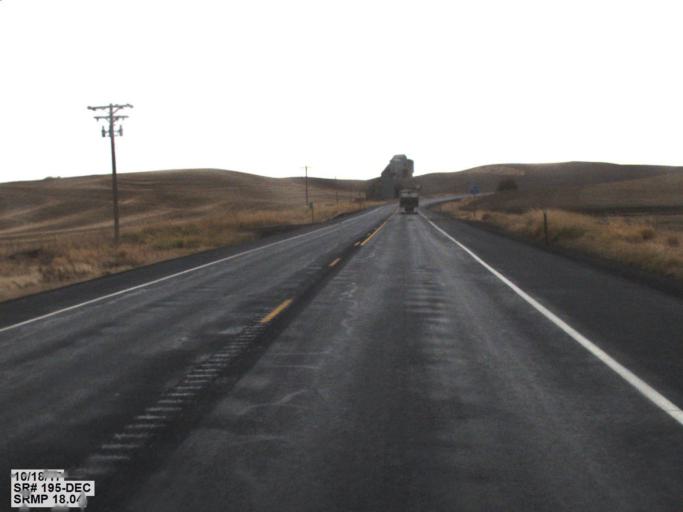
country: US
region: Washington
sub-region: Whitman County
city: Pullman
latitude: 46.6818
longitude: -117.1969
